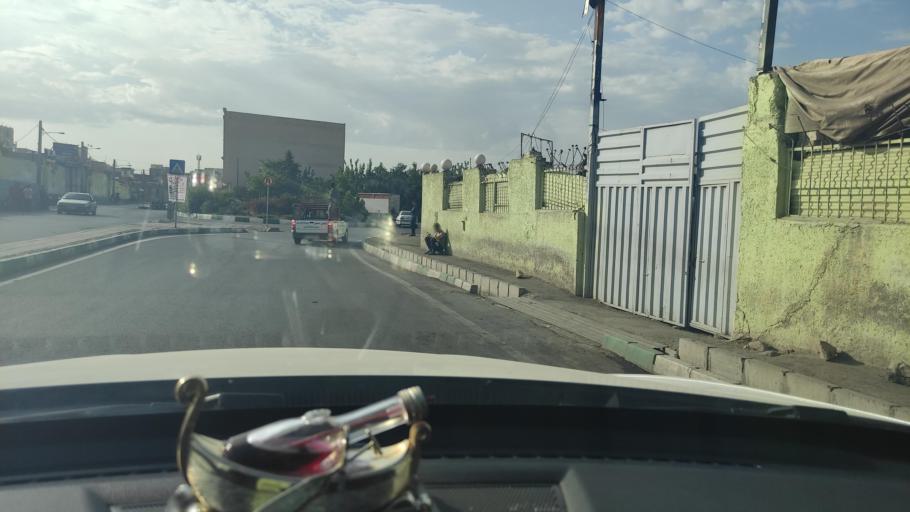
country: IR
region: Tehran
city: Tehran
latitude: 35.7526
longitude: 51.2798
